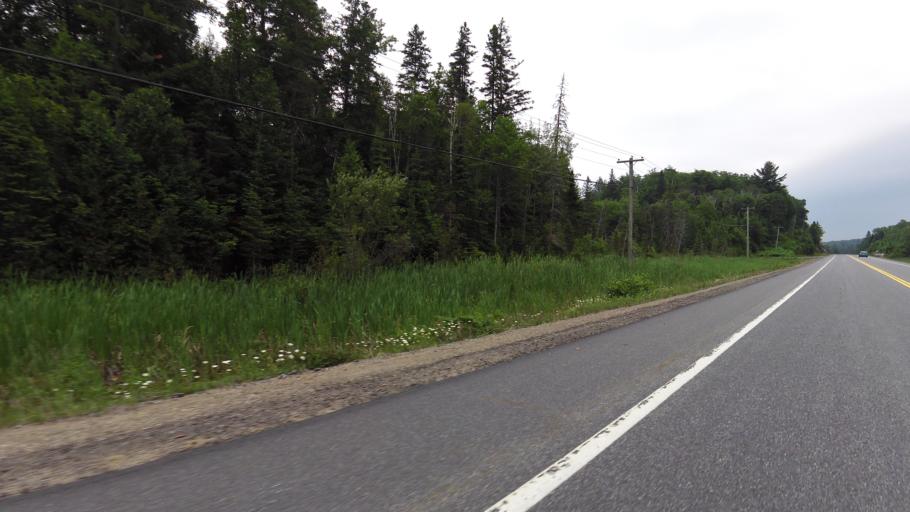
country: CA
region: Ontario
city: Huntsville
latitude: 45.4007
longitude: -78.8849
